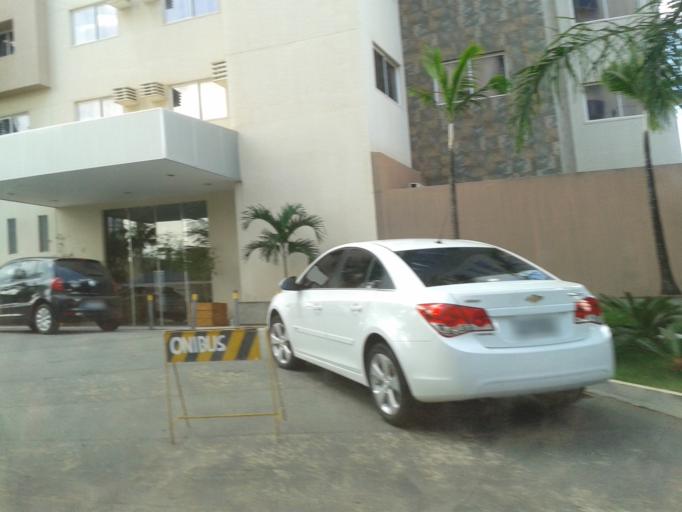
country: BR
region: Goias
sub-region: Caldas Novas
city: Caldas Novas
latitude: -17.7450
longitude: -48.6317
